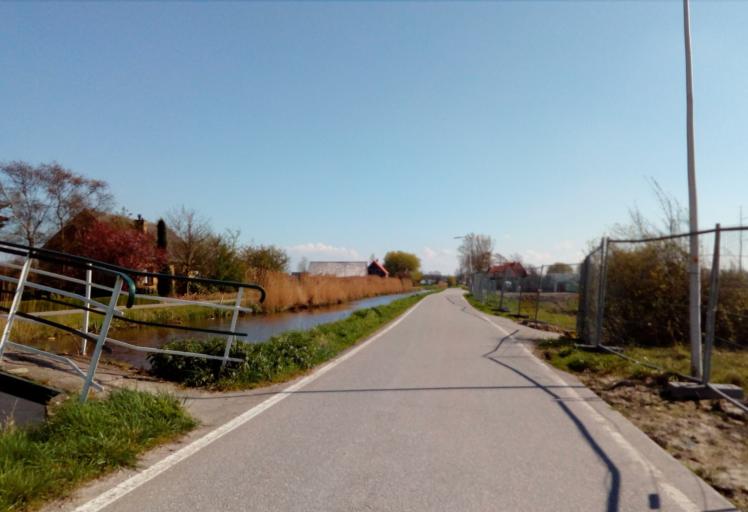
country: NL
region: South Holland
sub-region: Gemeente Rijswijk
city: Rijswijk
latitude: 52.0018
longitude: 4.3167
